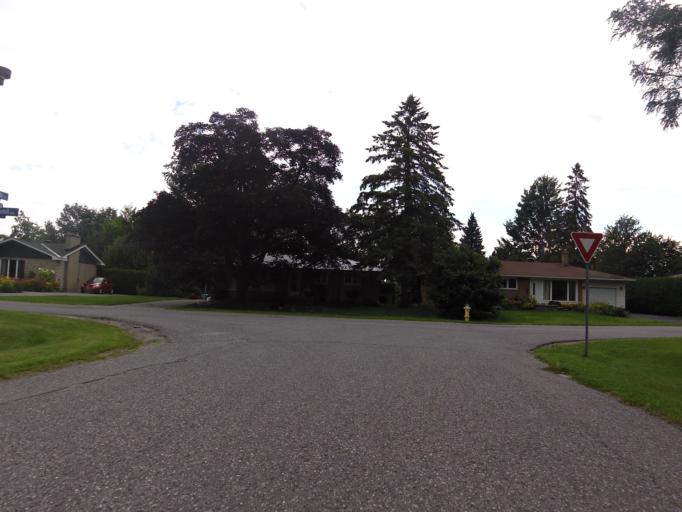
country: CA
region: Ontario
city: Bells Corners
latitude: 45.3287
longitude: -75.8102
